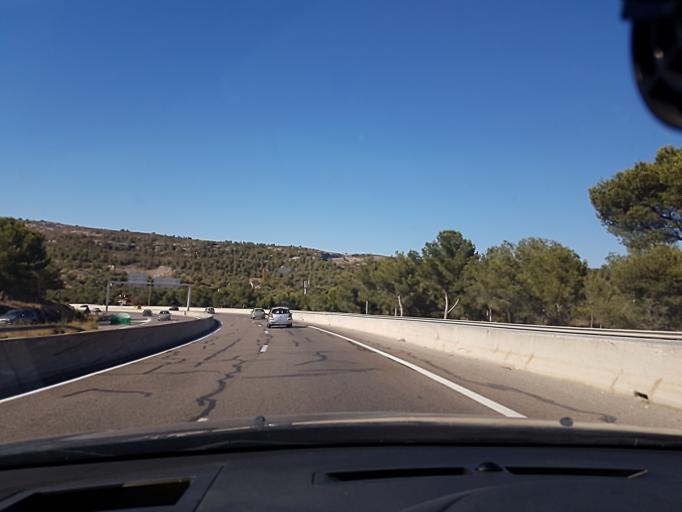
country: FR
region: Provence-Alpes-Cote d'Azur
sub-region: Departement des Bouches-du-Rhone
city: Ensues-la-Redonne
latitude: 43.3622
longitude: 5.1867
